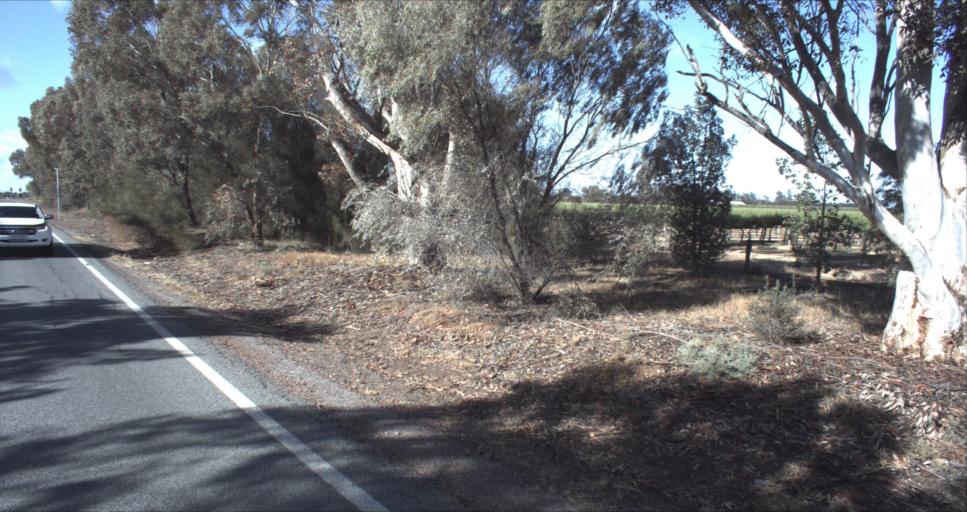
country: AU
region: New South Wales
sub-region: Leeton
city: Leeton
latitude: -34.5474
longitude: 146.3548
